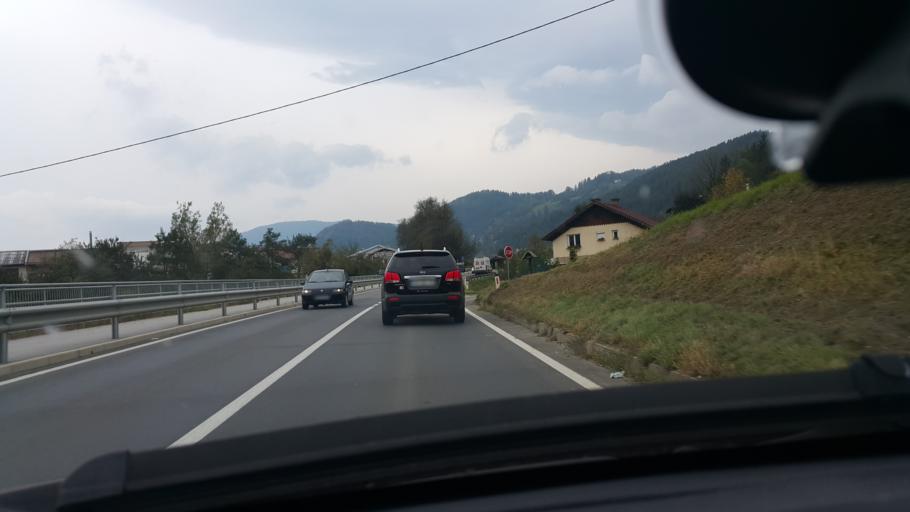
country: SI
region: Radlje ob Dravi
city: Radlje ob Dravi
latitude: 46.6053
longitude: 15.2509
